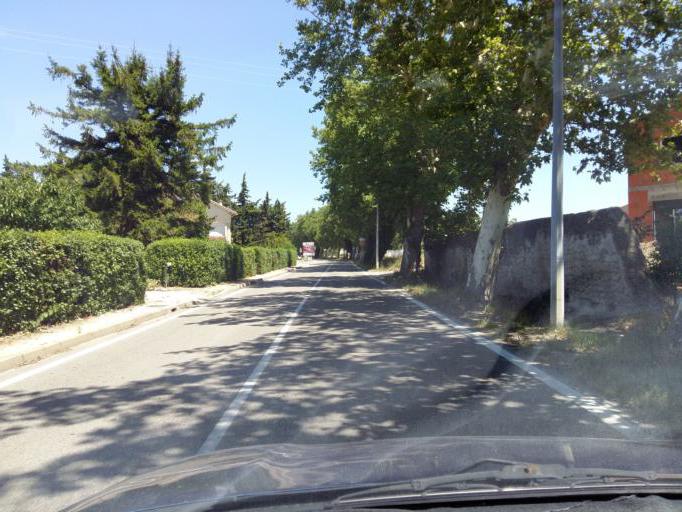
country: FR
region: Provence-Alpes-Cote d'Azur
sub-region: Departement du Vaucluse
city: Sainte-Cecile-les-Vignes
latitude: 44.2489
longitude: 4.8884
